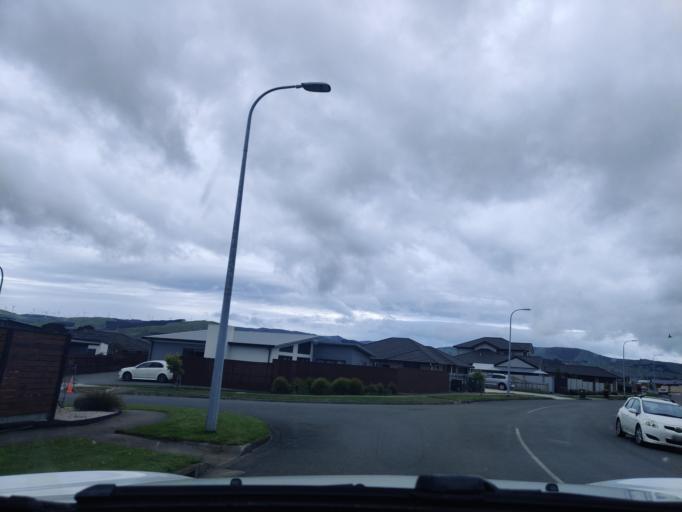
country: NZ
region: Manawatu-Wanganui
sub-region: Palmerston North City
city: Palmerston North
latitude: -40.3848
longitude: 175.6474
